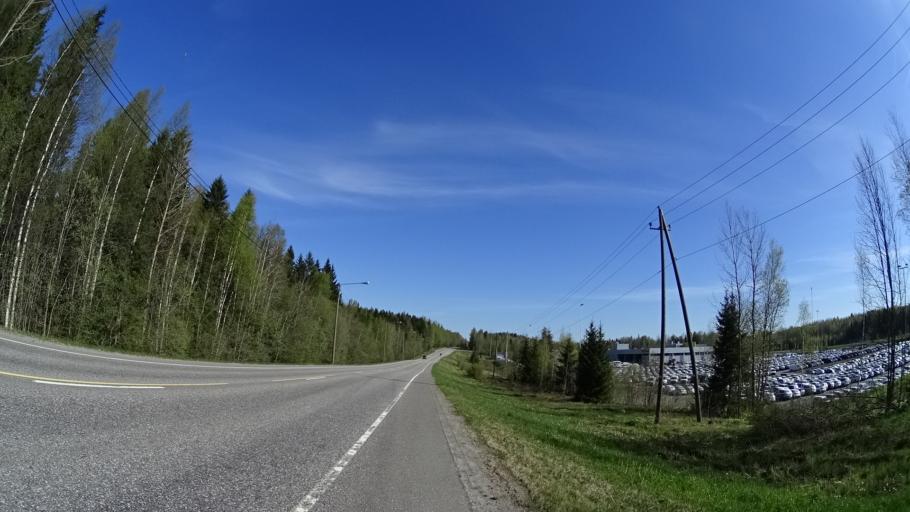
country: FI
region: Uusimaa
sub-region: Helsinki
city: Nurmijaervi
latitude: 60.3683
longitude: 24.8055
